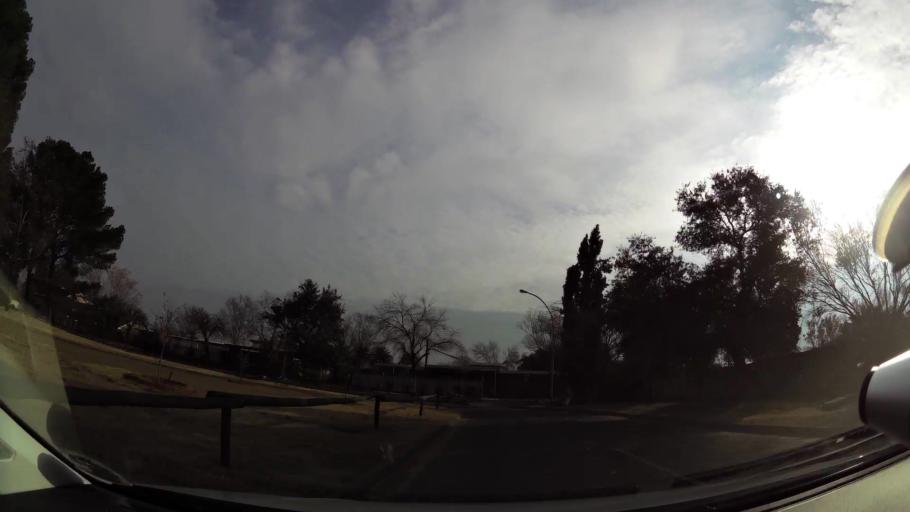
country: ZA
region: Orange Free State
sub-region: Mangaung Metropolitan Municipality
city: Bloemfontein
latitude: -29.1203
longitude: 26.1779
